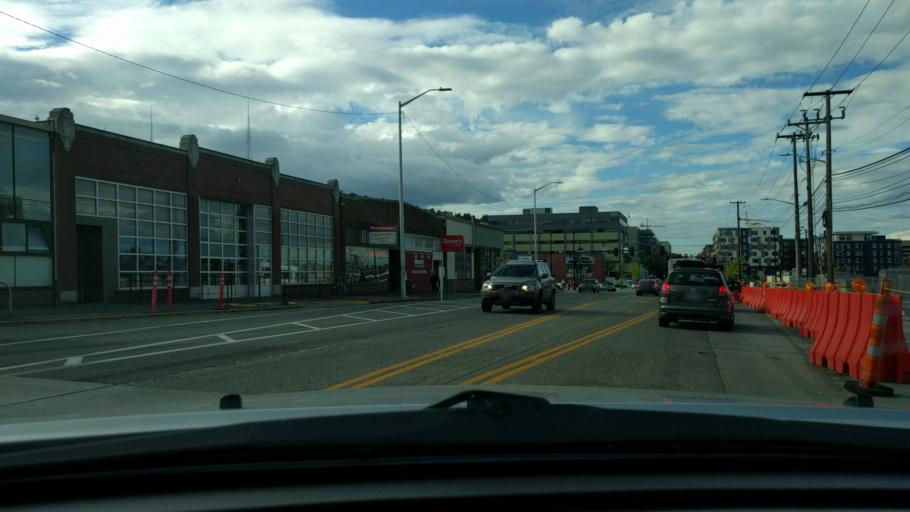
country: US
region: Washington
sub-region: King County
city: Seattle
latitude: 47.6233
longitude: -122.3424
